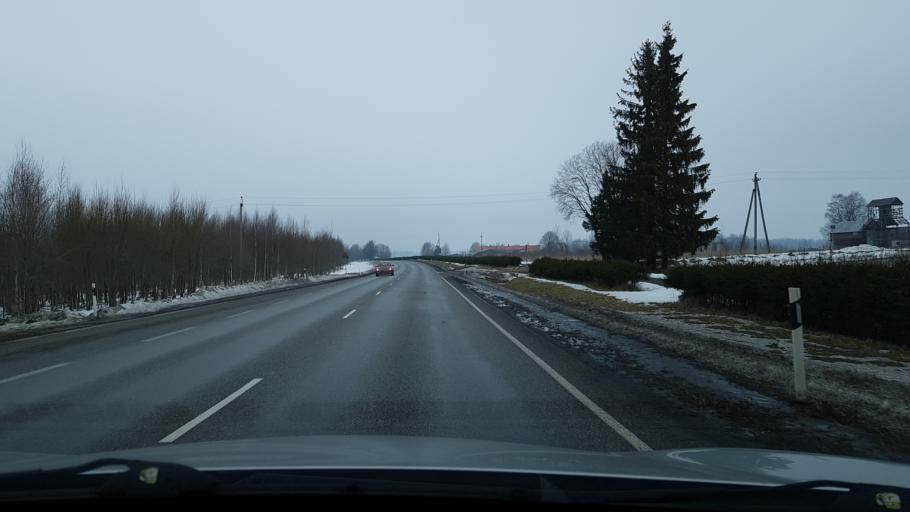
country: EE
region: Valgamaa
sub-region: Valga linn
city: Valga
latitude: 57.9271
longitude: 26.1754
